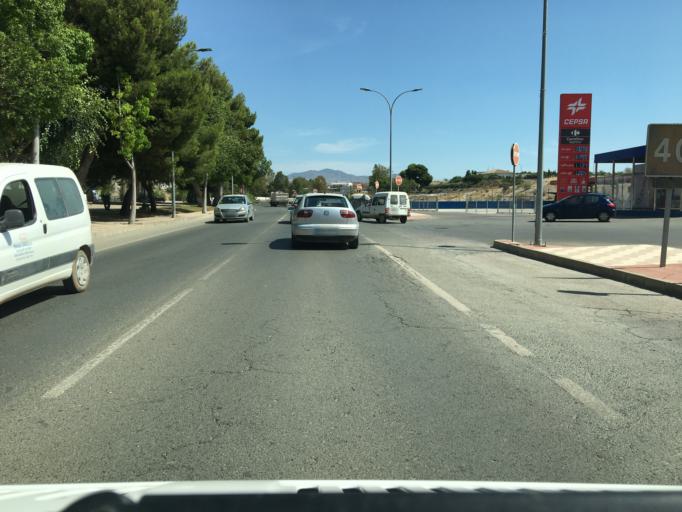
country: ES
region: Andalusia
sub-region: Provincia de Almeria
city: Huercal-Overa
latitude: 37.4015
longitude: -1.9388
